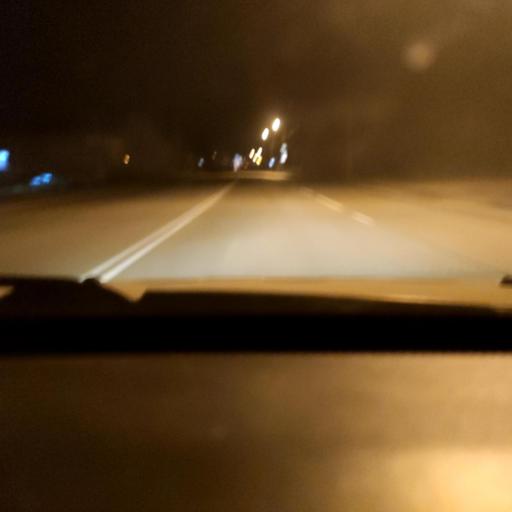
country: RU
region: Perm
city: Polazna
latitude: 58.1193
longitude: 56.4028
